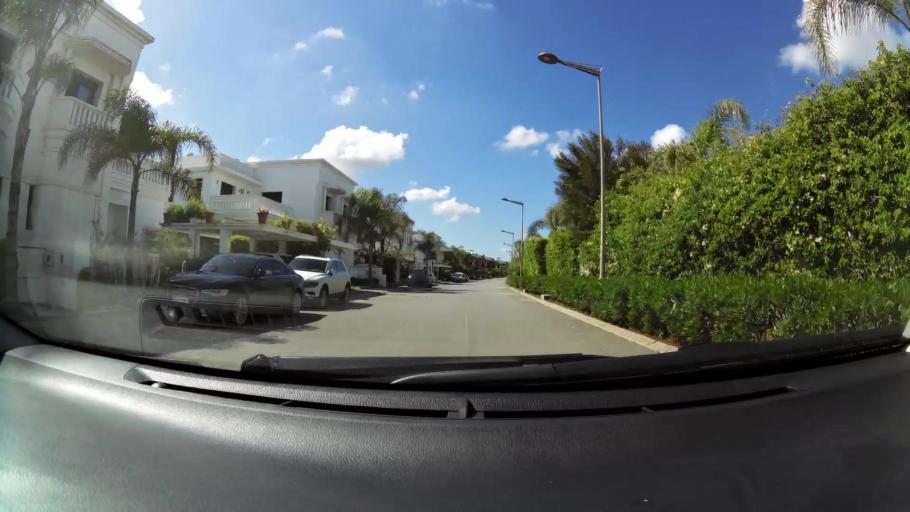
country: MA
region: Grand Casablanca
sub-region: Nouaceur
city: Bouskoura
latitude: 33.4682
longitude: -7.6081
